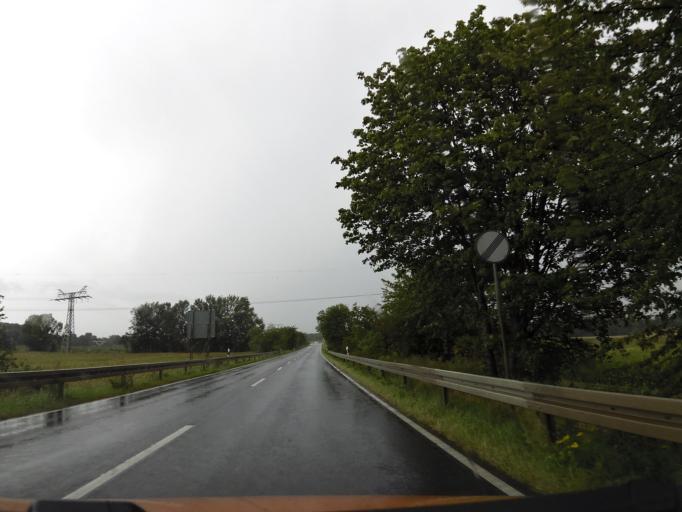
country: DE
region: Brandenburg
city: Werder
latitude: 52.4546
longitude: 12.9783
